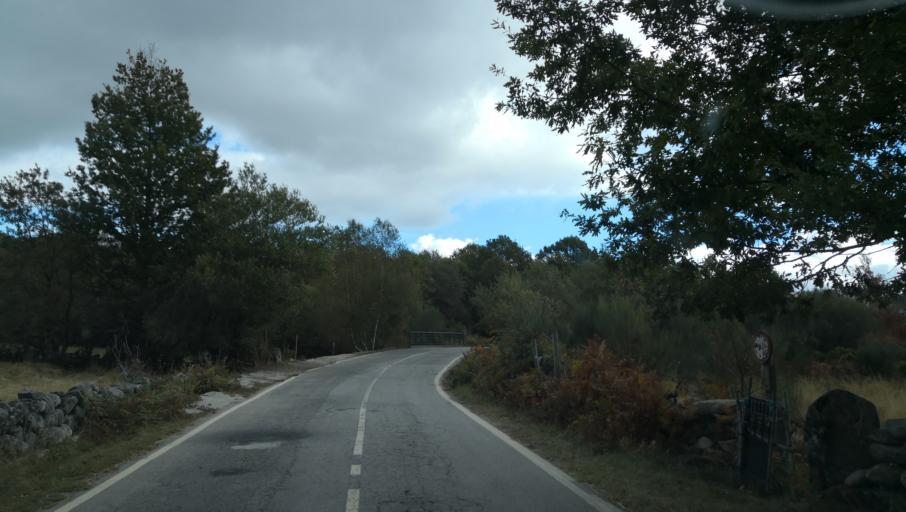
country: PT
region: Vila Real
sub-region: Vila Real
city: Vila Real
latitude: 41.3748
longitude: -7.8069
